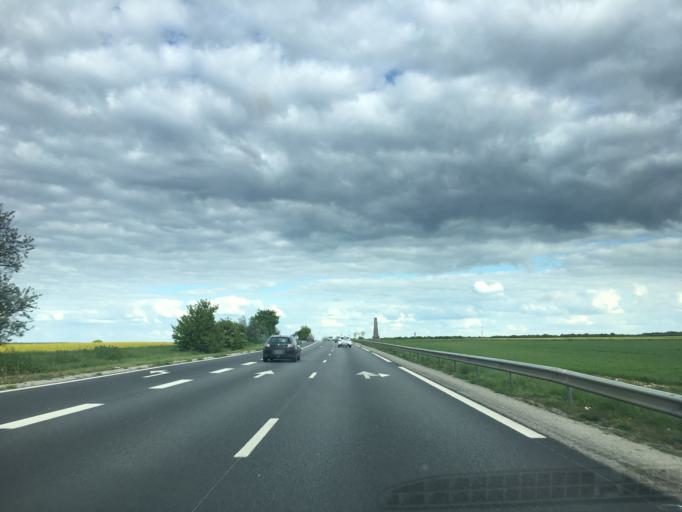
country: FR
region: Centre
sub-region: Departement d'Eure-et-Loir
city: Vert-en-Drouais
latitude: 48.7440
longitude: 1.2882
